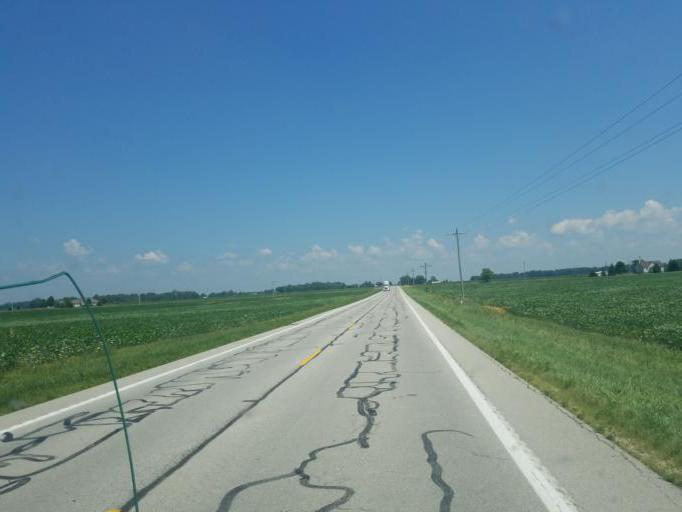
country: US
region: Ohio
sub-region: Shelby County
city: Anna
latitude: 40.3953
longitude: -84.1247
